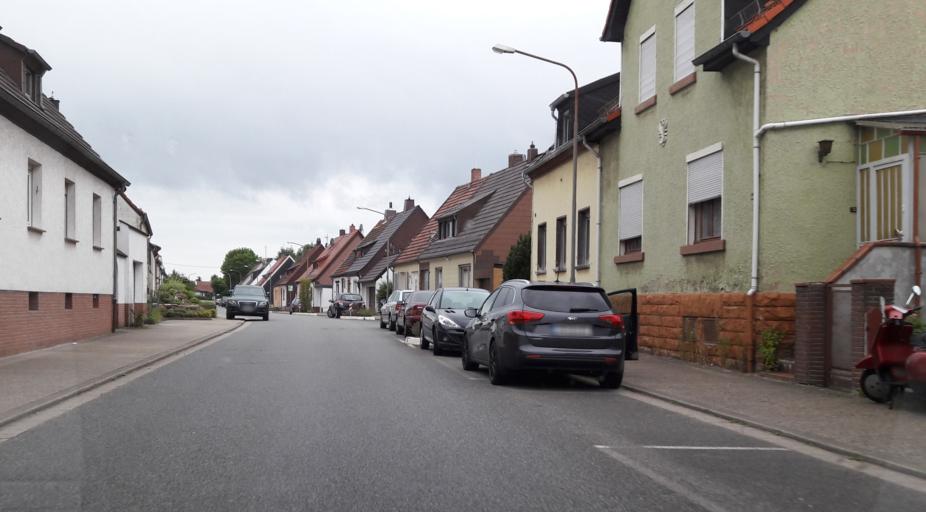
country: DE
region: Saarland
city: Spiesen-Elversberg
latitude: 49.3125
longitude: 7.1453
